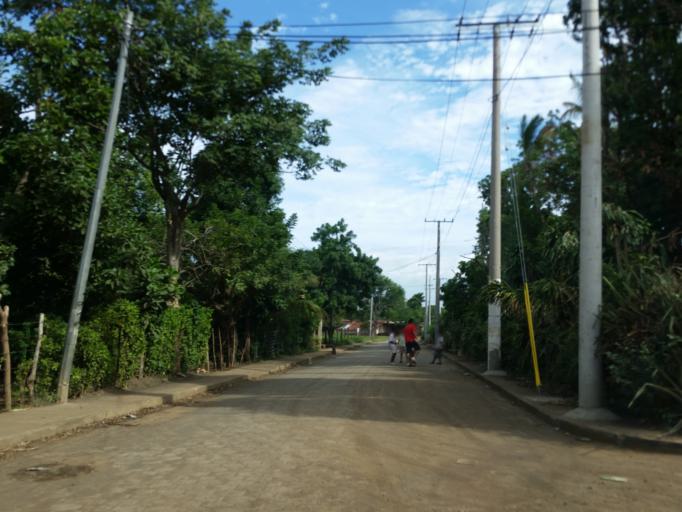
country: NI
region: Managua
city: Managua
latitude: 12.0857
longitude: -86.2267
